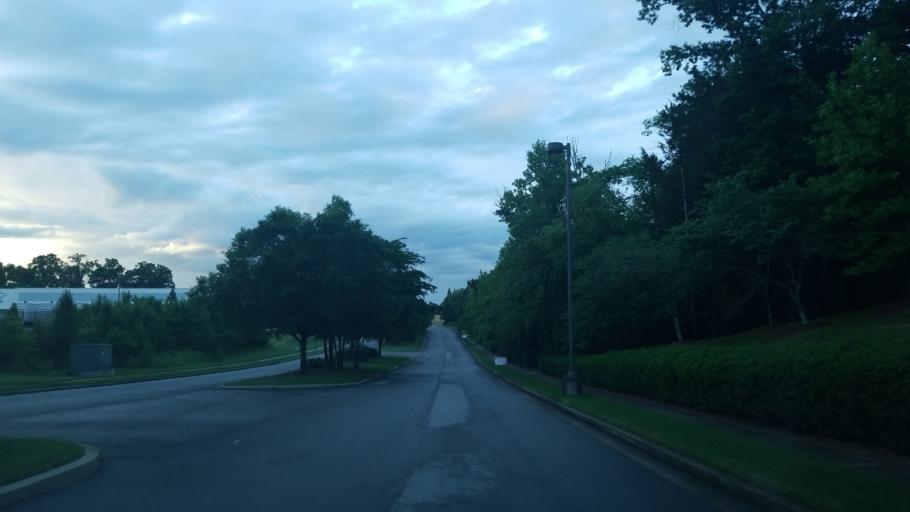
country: US
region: Tennessee
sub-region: Rutherford County
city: La Vergne
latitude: 36.1102
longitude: -86.6418
